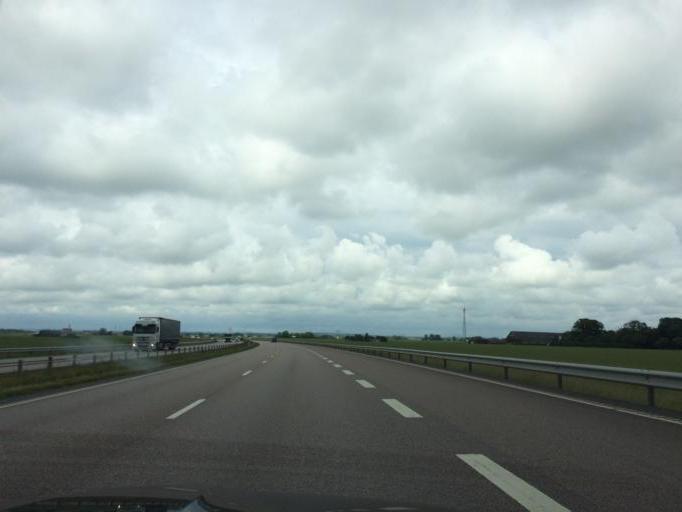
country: SE
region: Skane
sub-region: Helsingborg
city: Hyllinge
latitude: 56.1070
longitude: 12.8074
